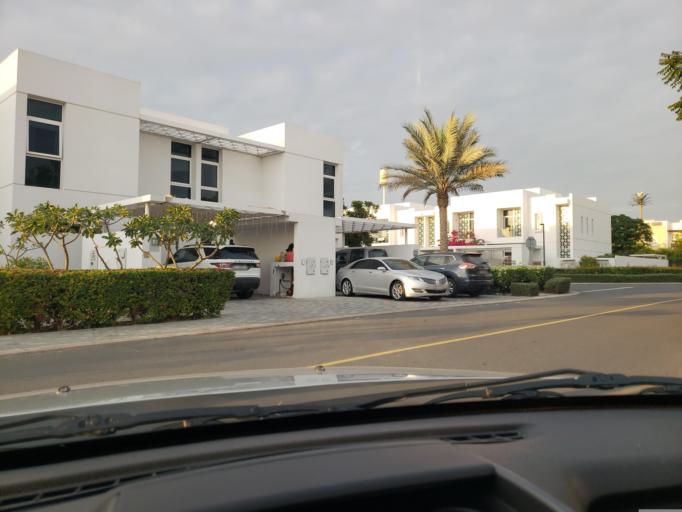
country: AE
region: Dubai
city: Dubai
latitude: 25.0191
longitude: 55.2741
